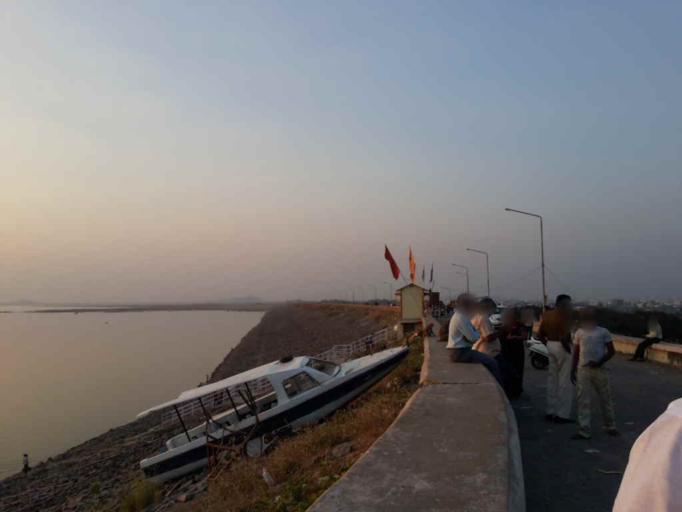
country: IN
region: Telangana
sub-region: Karimnagar
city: Karimnagar
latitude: 18.4019
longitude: 79.1296
